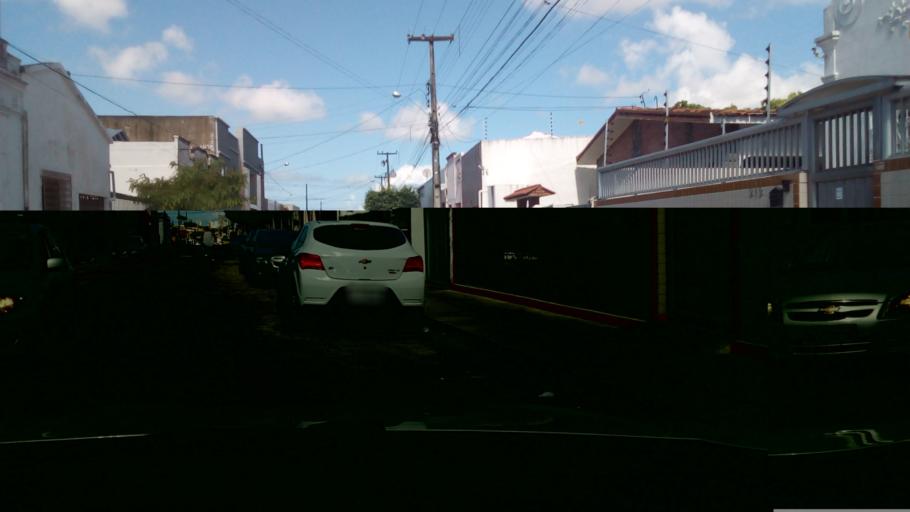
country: BR
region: Paraiba
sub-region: Joao Pessoa
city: Joao Pessoa
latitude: -7.1291
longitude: -34.8818
